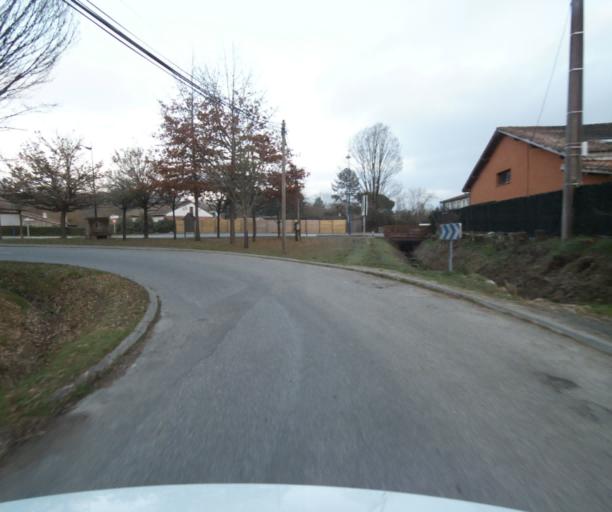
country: FR
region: Midi-Pyrenees
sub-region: Departement du Tarn-et-Garonne
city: Moissac
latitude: 44.1160
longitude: 1.1052
